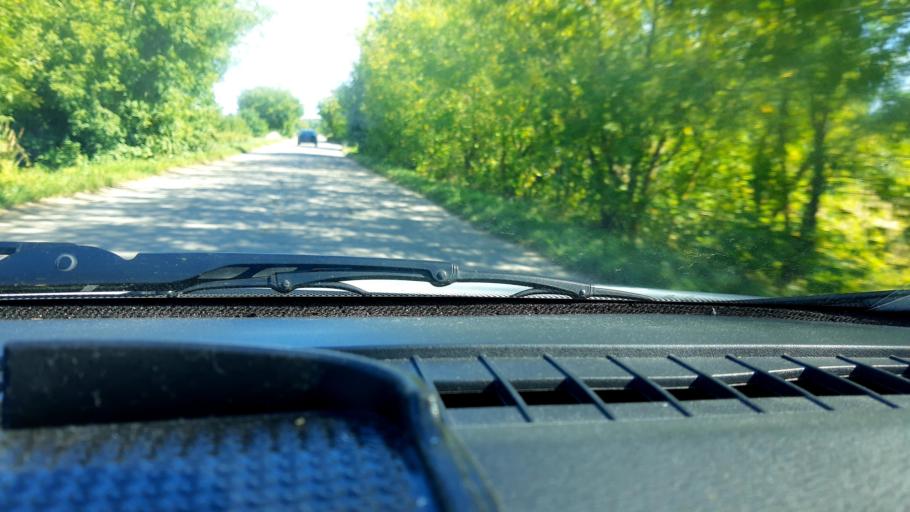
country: RU
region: Nizjnij Novgorod
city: Lukino
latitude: 56.4459
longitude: 43.6407
